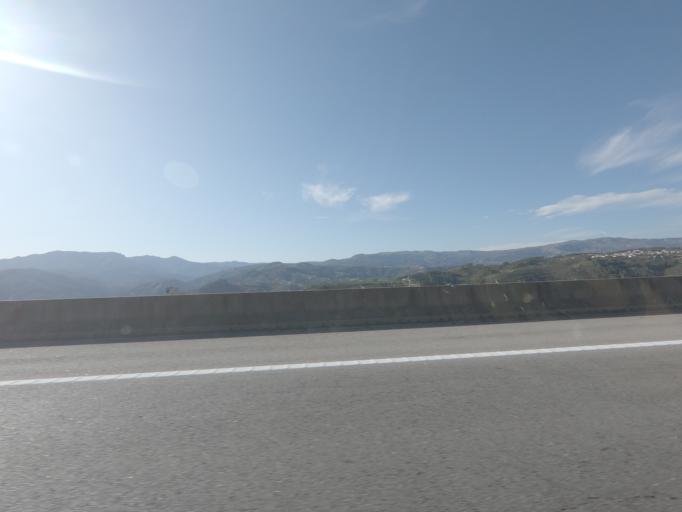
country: PT
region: Vila Real
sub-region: Vila Real
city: Vila Real
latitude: 41.2336
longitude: -7.7307
